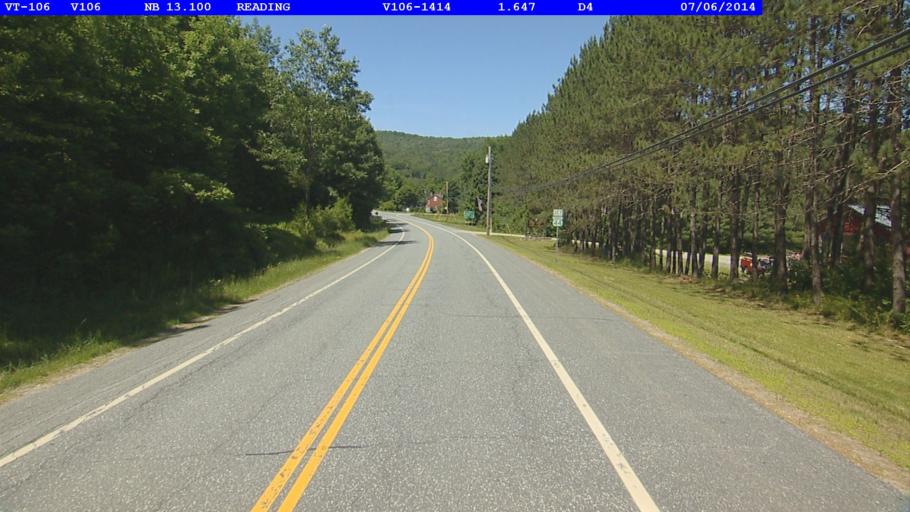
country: US
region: Vermont
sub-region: Windsor County
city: Windsor
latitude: 43.4673
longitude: -72.5330
